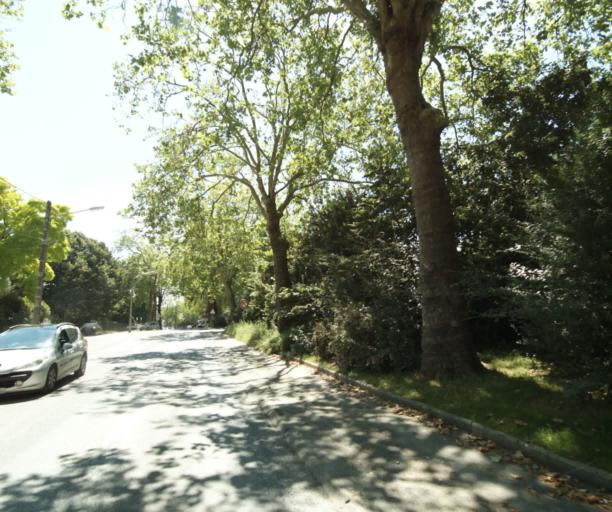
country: FR
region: Pays de la Loire
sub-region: Departement de la Mayenne
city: Laval
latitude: 48.0846
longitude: -0.7547
